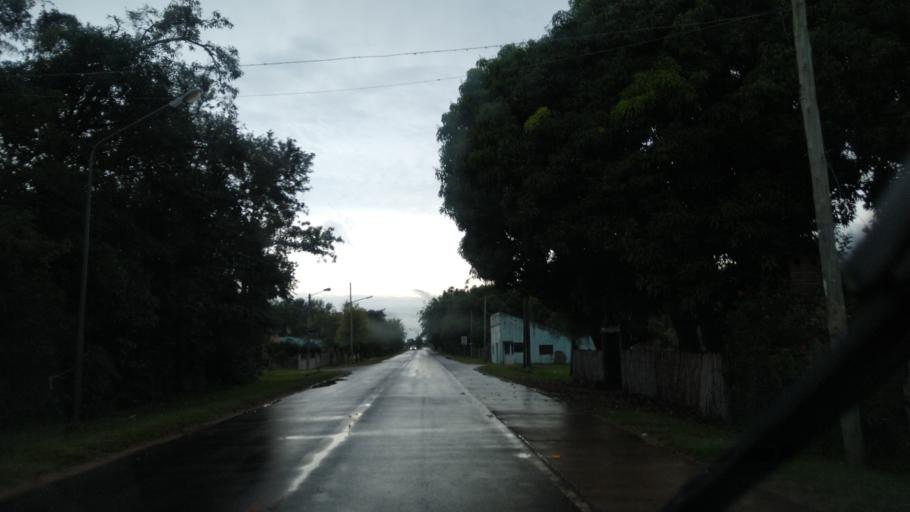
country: AR
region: Corrientes
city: Loreto
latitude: -27.7739
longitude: -57.2795
